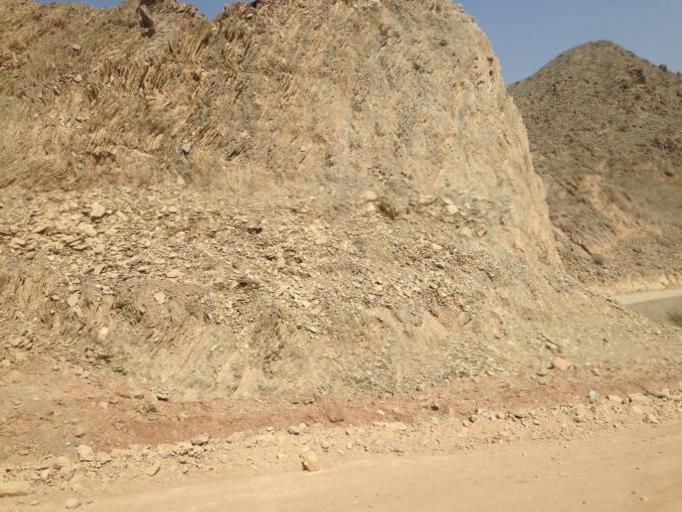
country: OM
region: Ash Sharqiyah
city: Al Qabil
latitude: 23.0686
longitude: 58.9593
